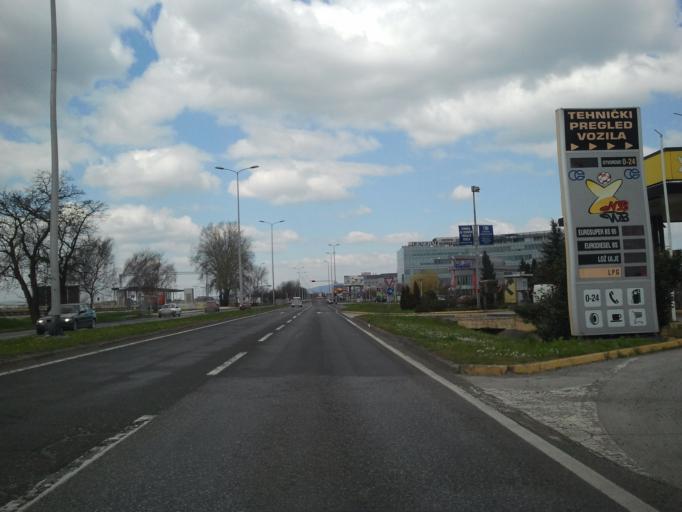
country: HR
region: Grad Zagreb
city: Odra
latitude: 45.7423
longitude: 16.0008
